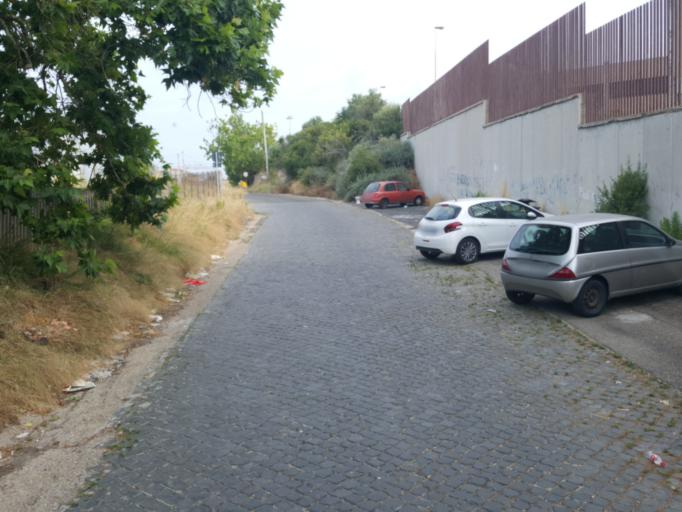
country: IT
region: Latium
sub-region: Citta metropolitana di Roma Capitale
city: Civitavecchia
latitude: 42.0987
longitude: 11.7911
